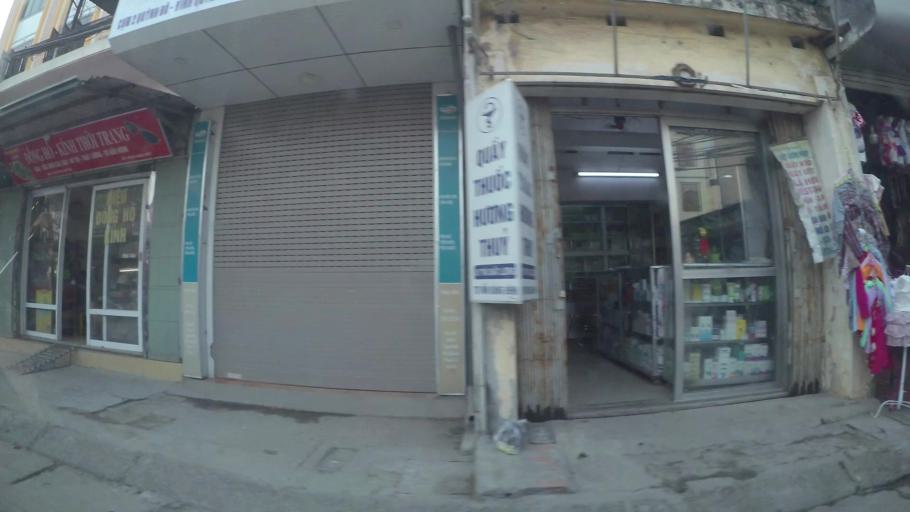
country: VN
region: Ha Noi
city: Van Dien
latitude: 20.9366
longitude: 105.8383
